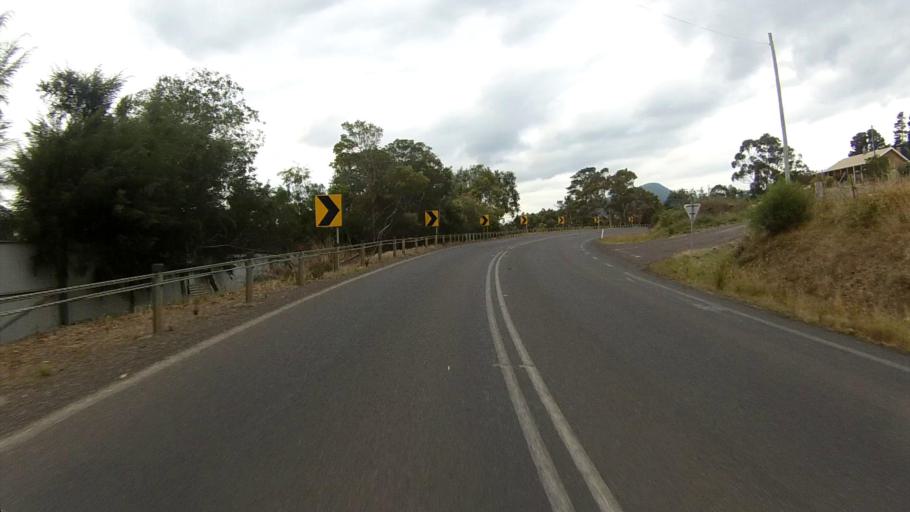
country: AU
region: Tasmania
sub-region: Huon Valley
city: Franklin
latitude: -43.0904
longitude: 147.0239
